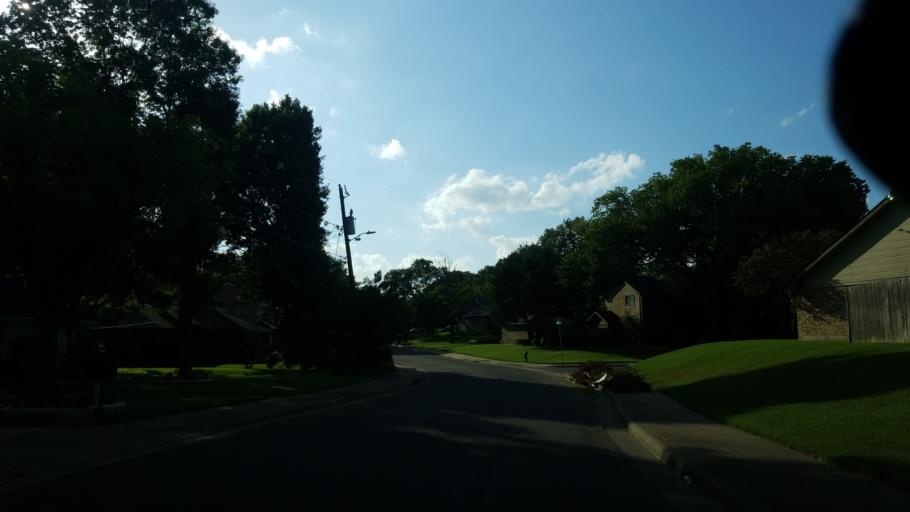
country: US
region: Texas
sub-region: Dallas County
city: Dallas
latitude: 32.7814
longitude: -96.7102
